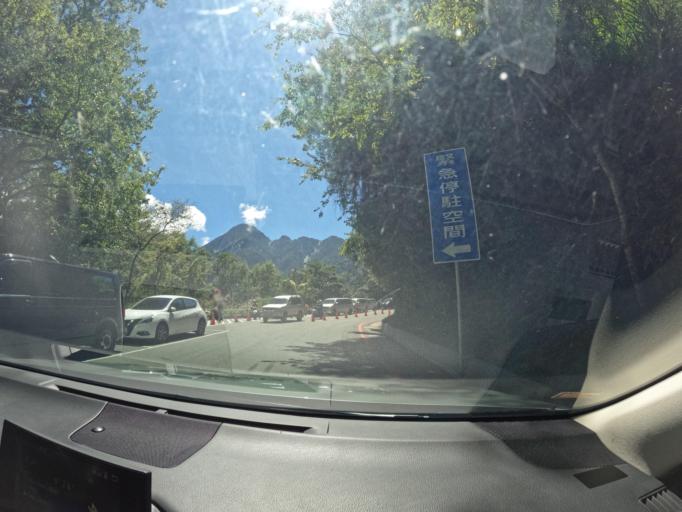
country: TW
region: Taiwan
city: Yujing
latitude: 23.2775
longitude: 120.9173
